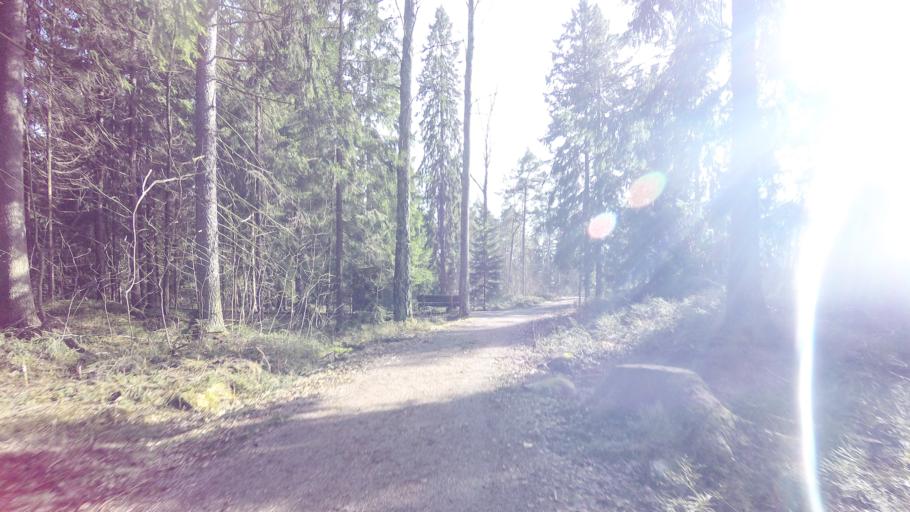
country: FI
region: Uusimaa
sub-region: Helsinki
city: Helsinki
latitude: 60.1973
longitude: 25.0137
